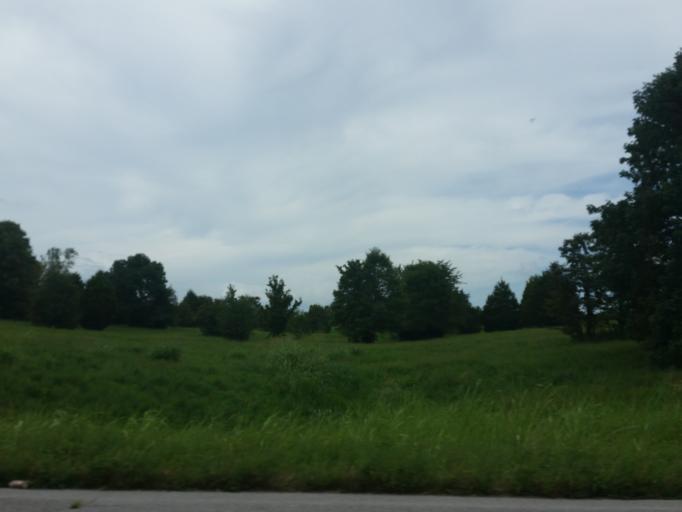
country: US
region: Kentucky
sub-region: Trigg County
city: Cadiz
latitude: 36.9505
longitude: -87.8443
